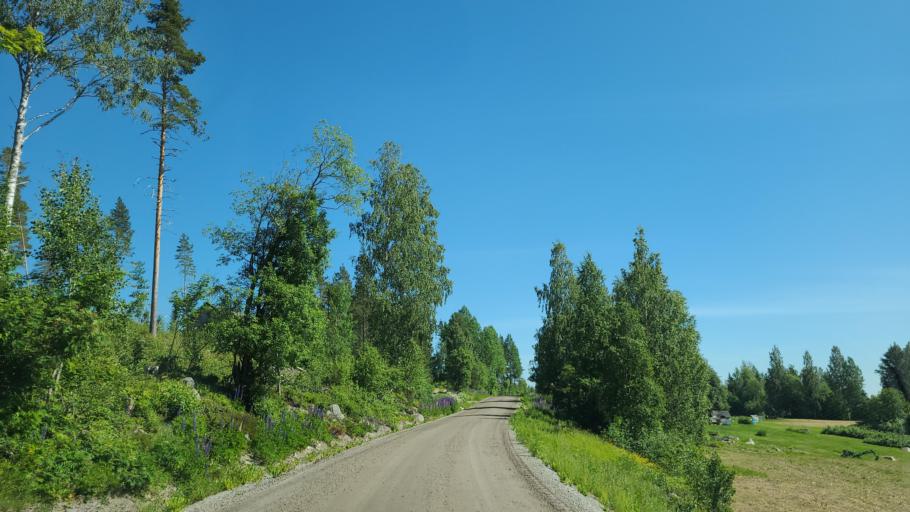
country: SE
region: Vaesterbotten
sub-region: Bjurholms Kommun
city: Bjurholm
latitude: 63.6751
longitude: 19.0240
